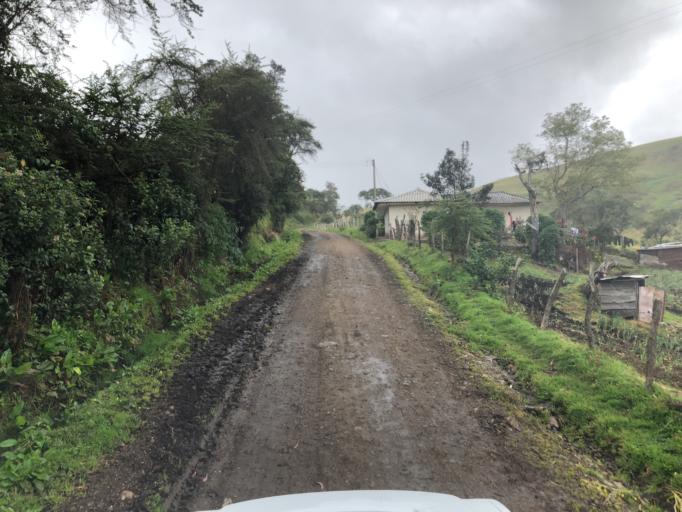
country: CO
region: Cauca
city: Totoro
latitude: 2.4706
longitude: -76.3265
